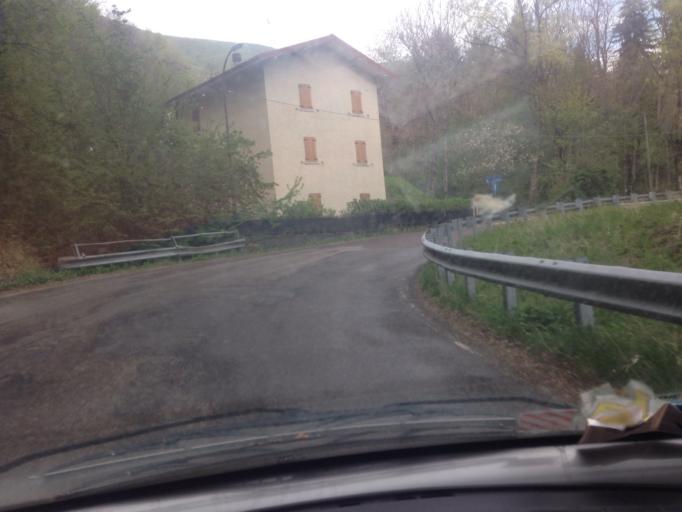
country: IT
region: Emilia-Romagna
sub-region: Provincia di Bologna
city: Lizzano in Belvedere
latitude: 44.1656
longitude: 10.8848
